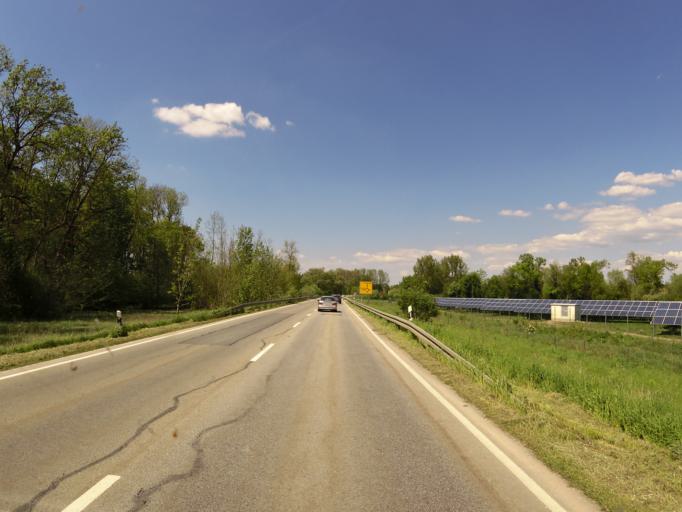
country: DE
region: Bavaria
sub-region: Lower Bavaria
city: Plattling
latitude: 48.7646
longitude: 12.8939
